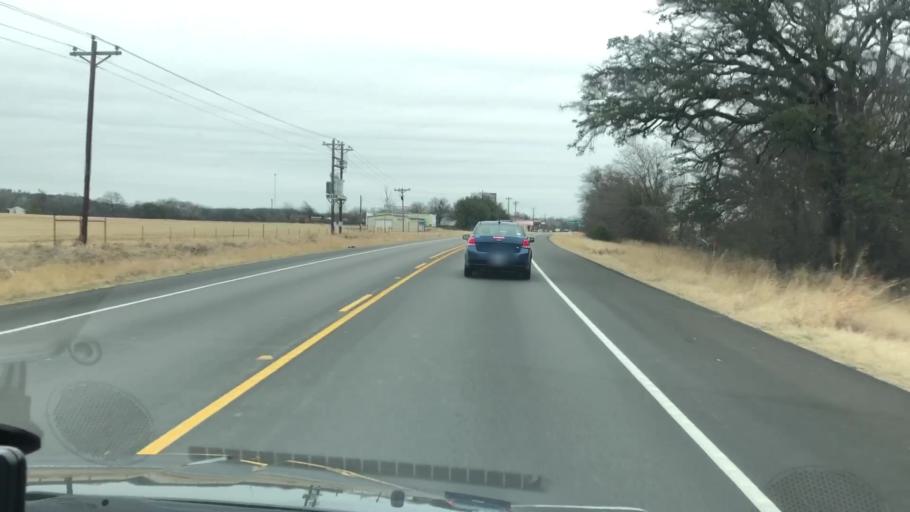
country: US
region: Texas
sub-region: Erath County
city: Stephenville
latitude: 32.3810
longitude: -98.1714
